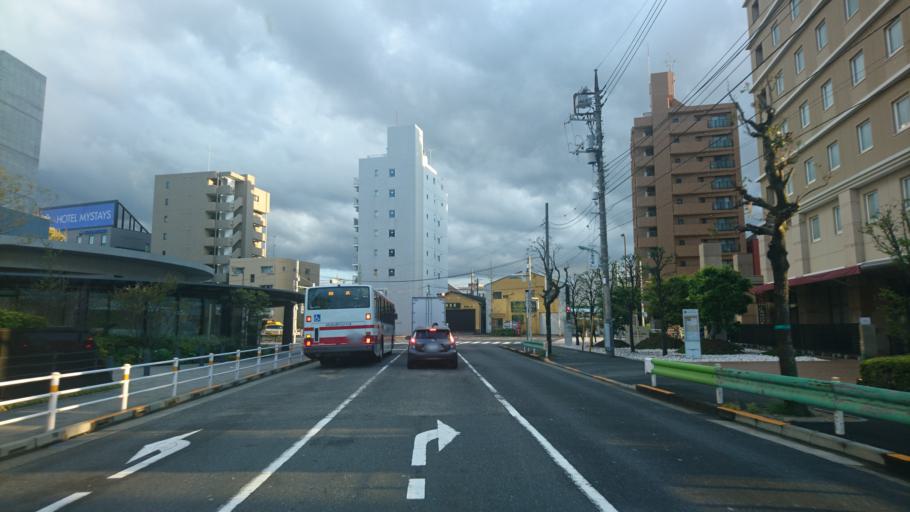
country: JP
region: Kanagawa
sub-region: Kawasaki-shi
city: Kawasaki
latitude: 35.5520
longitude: 139.7484
